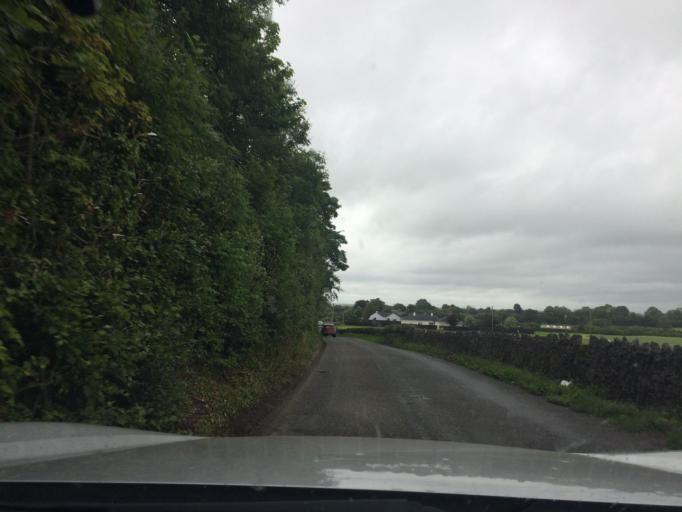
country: IE
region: Munster
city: Thurles
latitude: 52.6263
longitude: -7.8753
